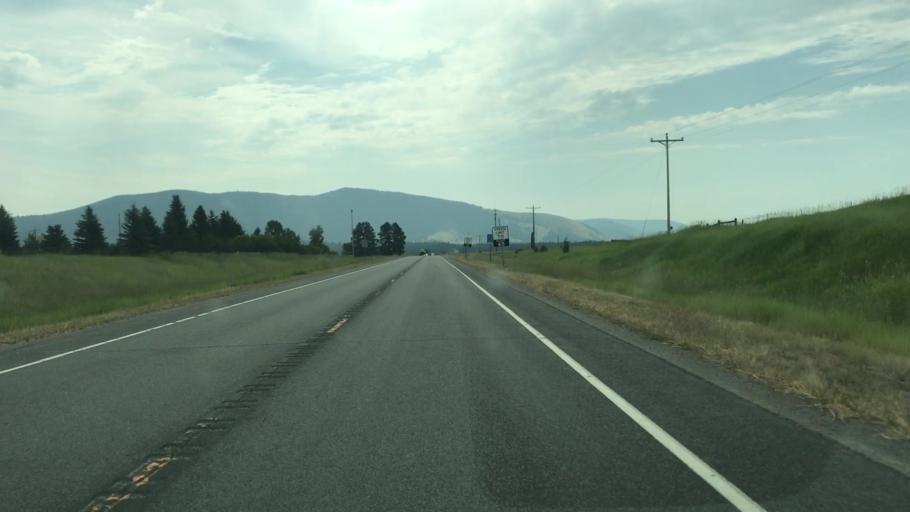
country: US
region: Montana
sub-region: Lewis and Clark County
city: Lincoln
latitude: 46.9980
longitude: -113.0316
